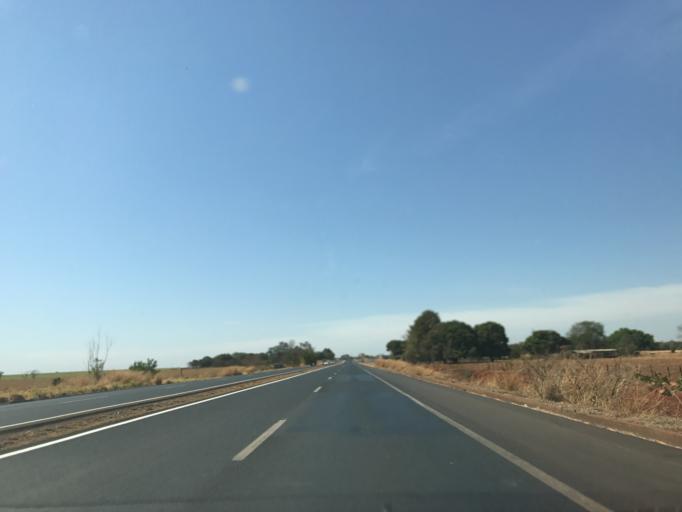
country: BR
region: Minas Gerais
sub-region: Centralina
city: Centralina
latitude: -18.7409
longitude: -49.0967
